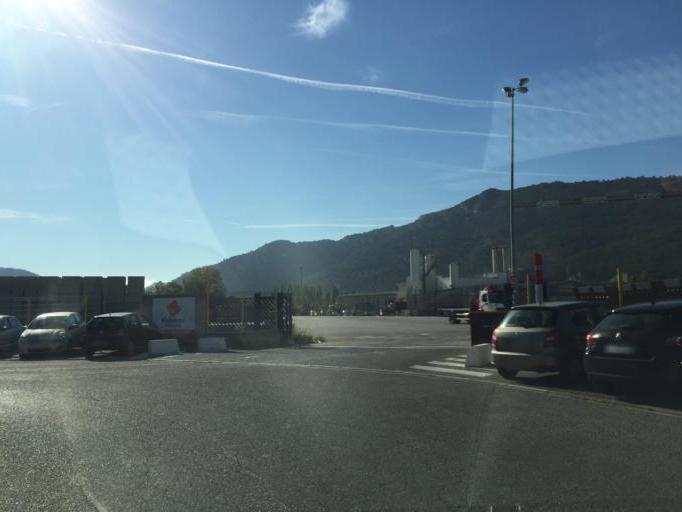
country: FR
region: Provence-Alpes-Cote d'Azur
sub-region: Departement des Bouches-du-Rhone
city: Gemenos
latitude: 43.2863
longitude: 5.6065
